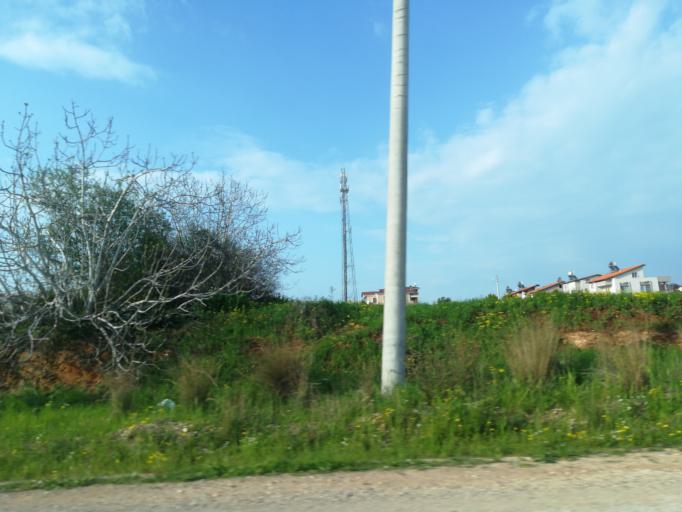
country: TR
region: Adana
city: Adana
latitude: 37.0778
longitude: 35.3933
